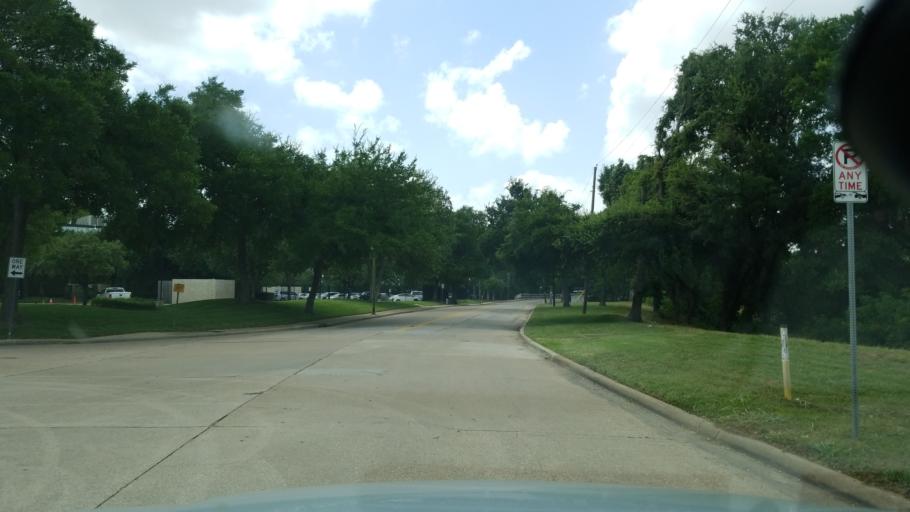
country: US
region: Texas
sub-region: Dallas County
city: Dallas
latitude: 32.8176
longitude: -96.8631
